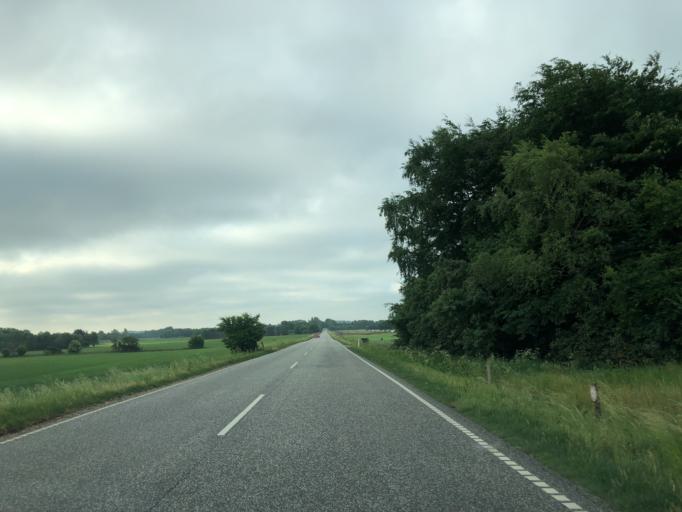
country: DK
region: South Denmark
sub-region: Vejle Kommune
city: Give
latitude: 55.8763
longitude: 9.2315
